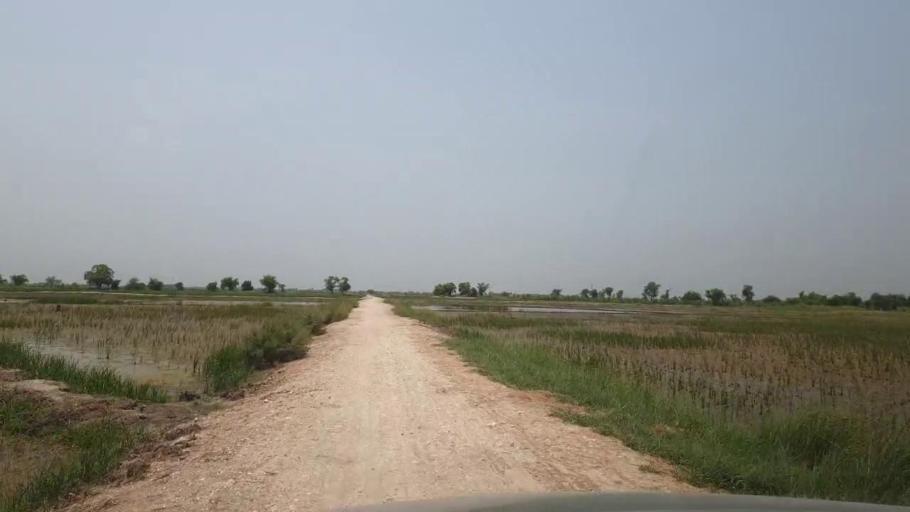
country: PK
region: Sindh
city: Garhi Yasin
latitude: 27.8646
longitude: 68.4836
